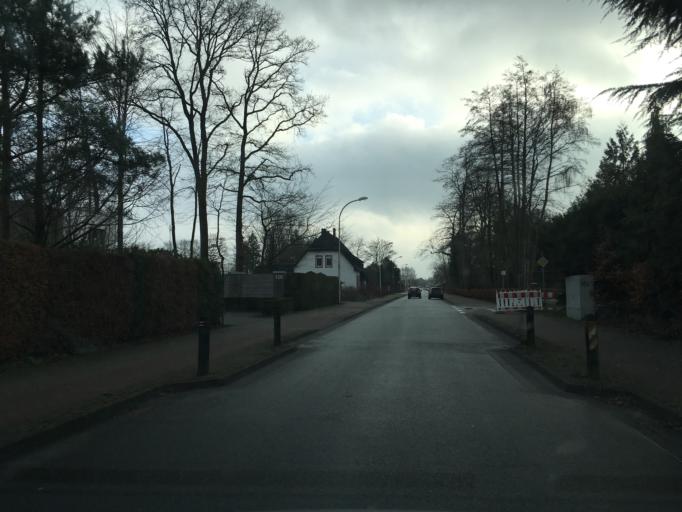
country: DE
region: North Rhine-Westphalia
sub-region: Regierungsbezirk Munster
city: Gronau
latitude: 52.2250
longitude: 7.0100
